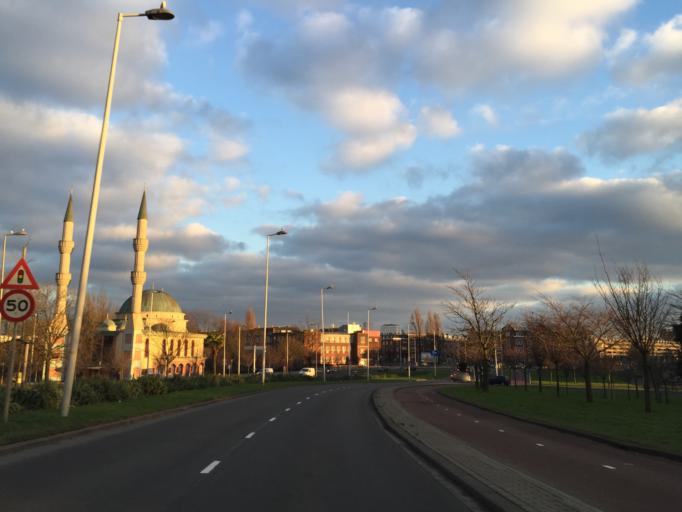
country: NL
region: South Holland
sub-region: Gemeente Rotterdam
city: Delfshaven
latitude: 51.9214
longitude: 4.4394
